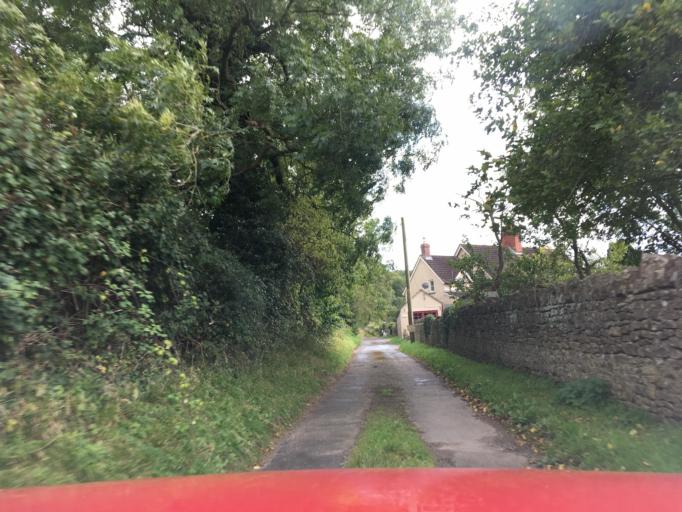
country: GB
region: England
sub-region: South Gloucestershire
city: Falfield
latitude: 51.6257
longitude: -2.4530
